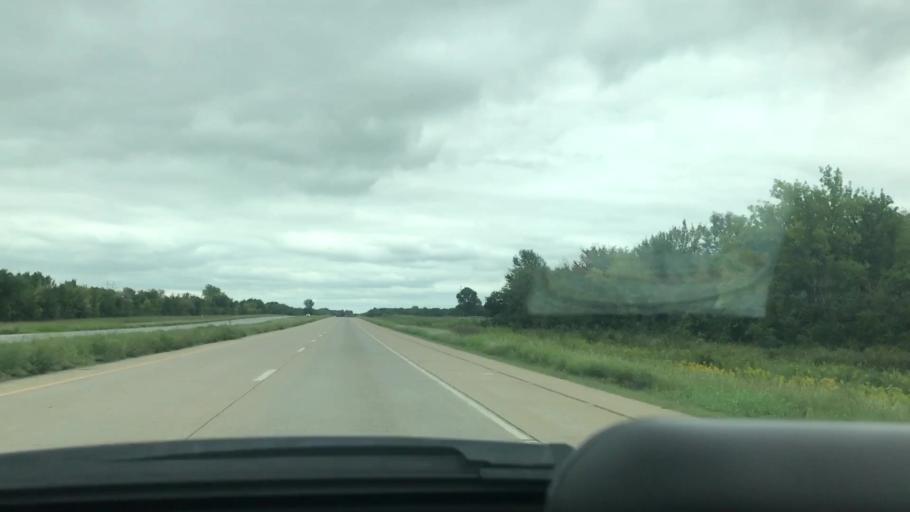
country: US
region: Oklahoma
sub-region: Mayes County
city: Chouteau
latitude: 36.2092
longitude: -95.3408
